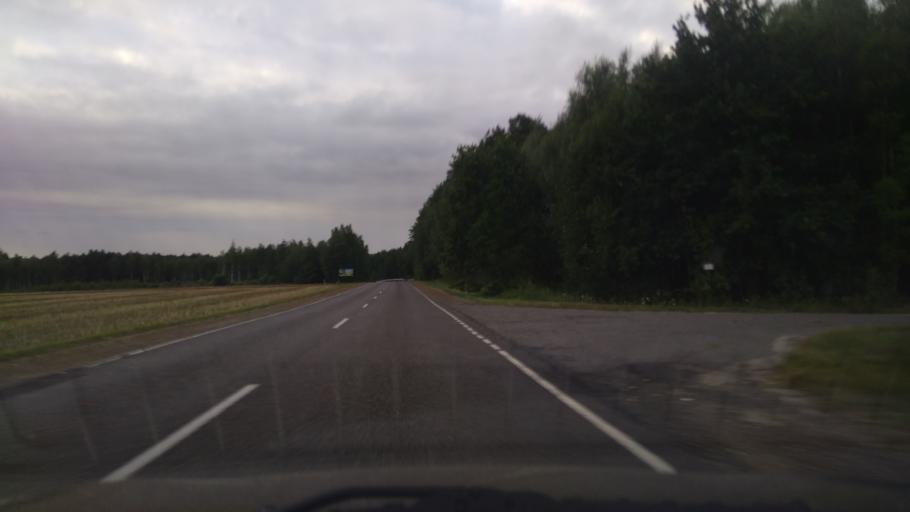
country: BY
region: Brest
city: Byaroza
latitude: 52.4026
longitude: 25.0020
